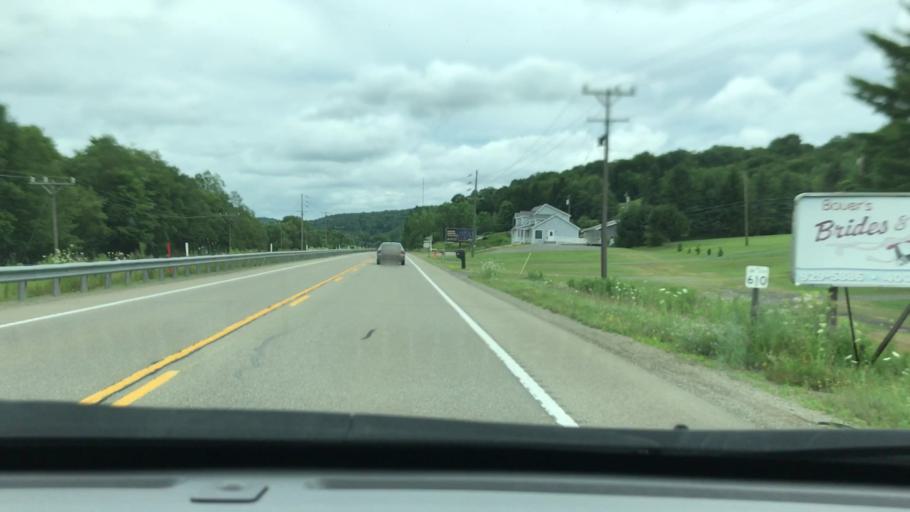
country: US
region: Pennsylvania
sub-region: Elk County
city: Johnsonburg
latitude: 41.5434
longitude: -78.6812
